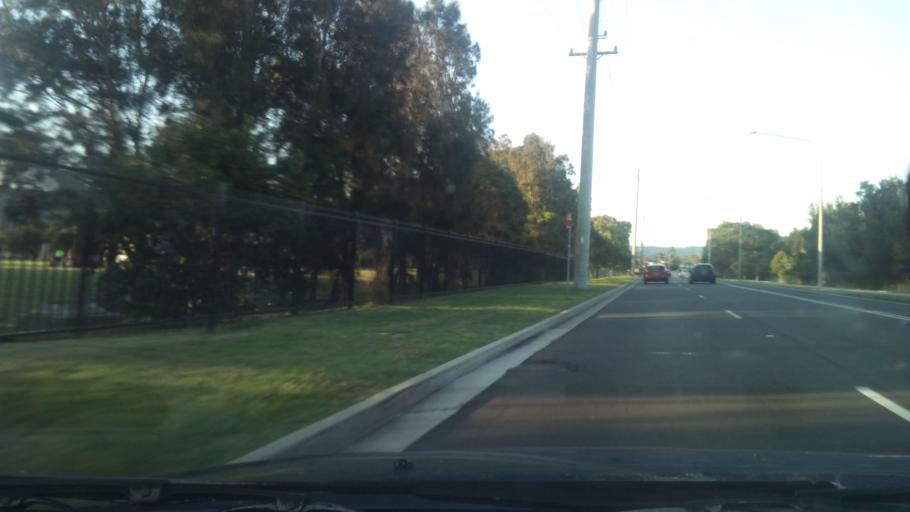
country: AU
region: New South Wales
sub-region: Wollongong
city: Fairy Meadow
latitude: -34.3987
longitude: 150.9009
